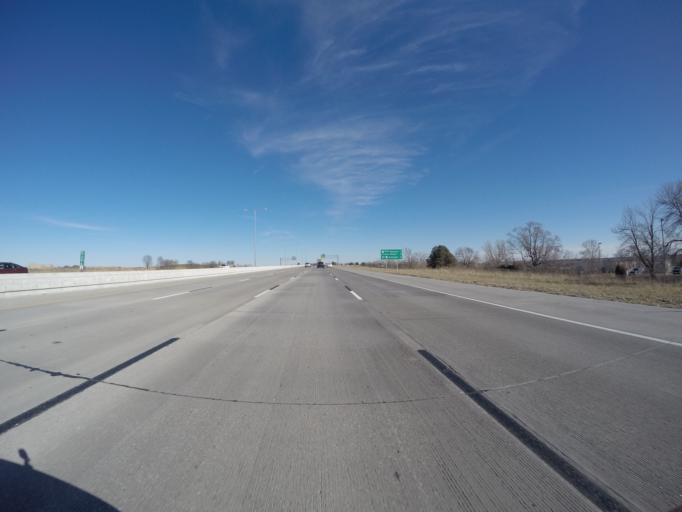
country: US
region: Nebraska
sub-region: Lancaster County
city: Lincoln
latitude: 40.8159
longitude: -96.7733
